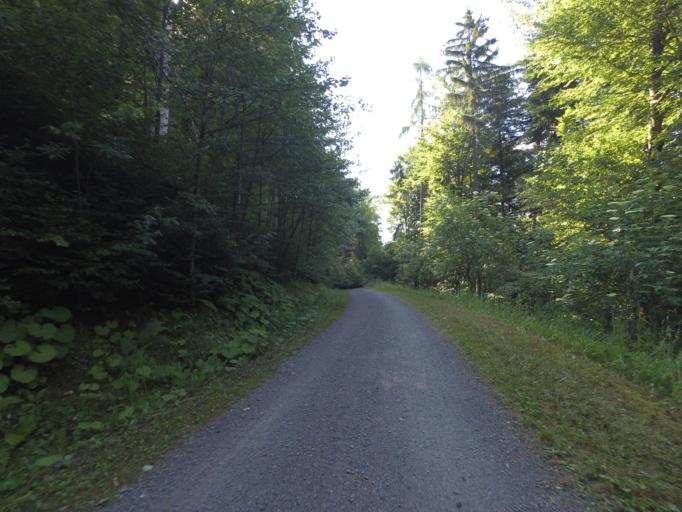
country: AT
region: Carinthia
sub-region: Politischer Bezirk Spittal an der Drau
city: Millstatt
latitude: 46.7890
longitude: 13.5805
